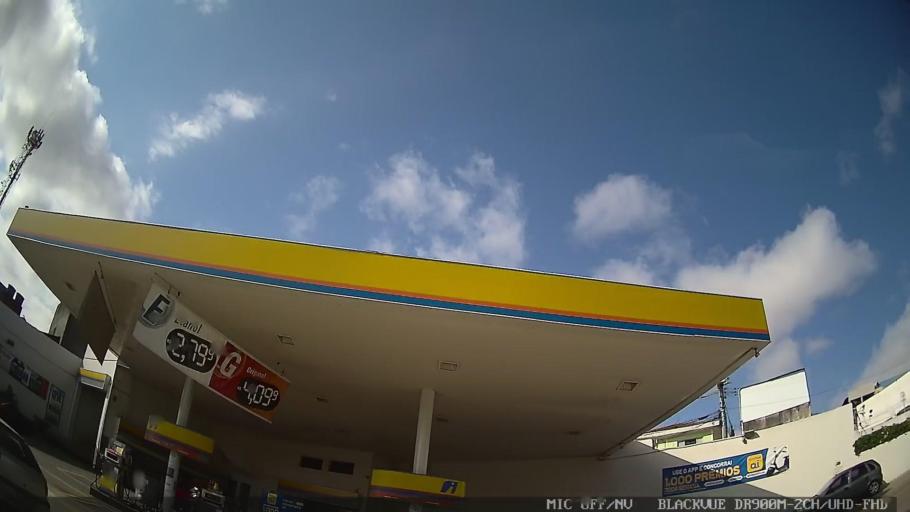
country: BR
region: Sao Paulo
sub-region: Guarulhos
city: Guarulhos
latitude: -23.5428
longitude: -46.4962
